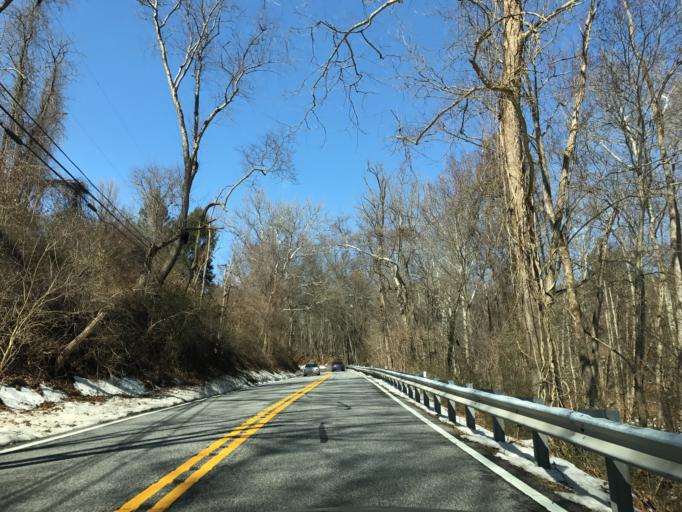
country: US
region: Maryland
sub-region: Carroll County
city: Hampstead
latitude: 39.5591
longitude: -76.7464
